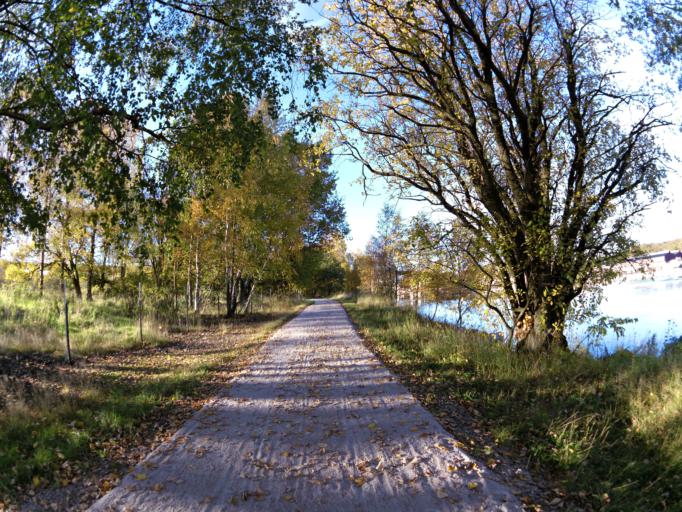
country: NO
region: Ostfold
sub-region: Sarpsborg
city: Sarpsborg
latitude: 59.2660
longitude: 11.1007
